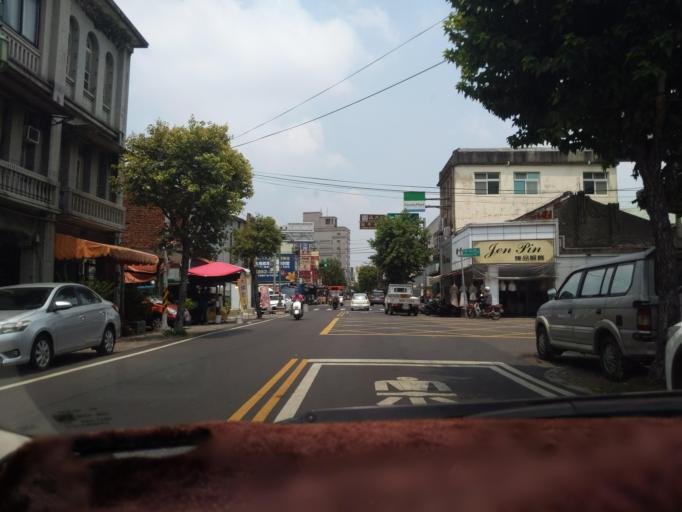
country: TW
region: Taiwan
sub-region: Yunlin
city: Douliu
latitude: 23.8010
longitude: 120.4587
